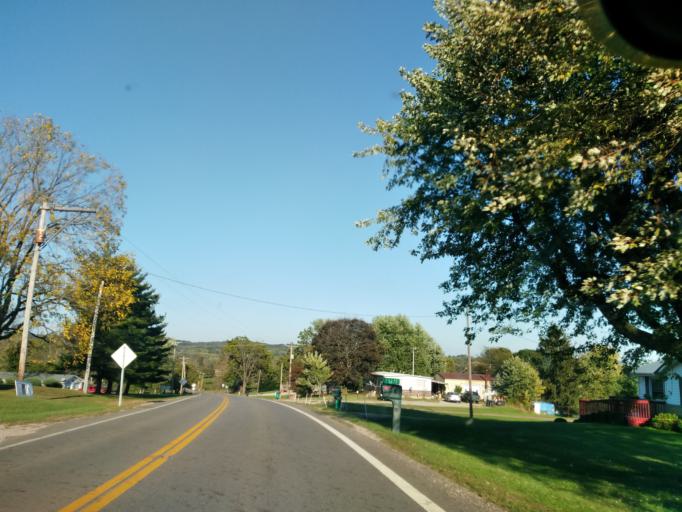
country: US
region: Ohio
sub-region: Ross County
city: Kingston
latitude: 39.5509
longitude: -82.7894
